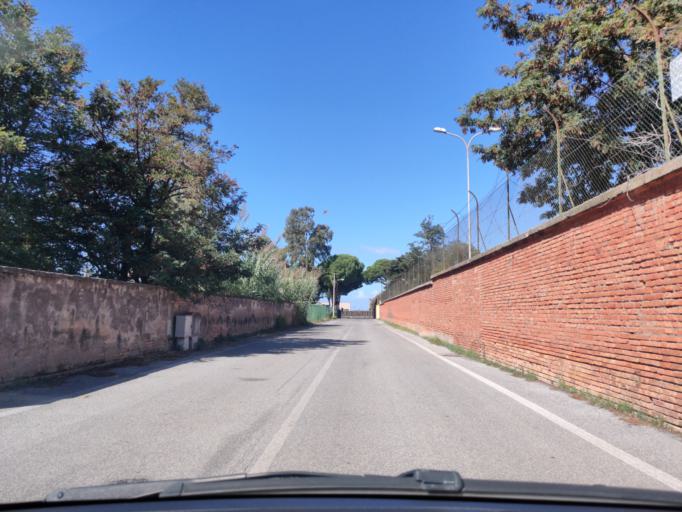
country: IT
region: Latium
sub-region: Citta metropolitana di Roma Capitale
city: Aurelia
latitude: 42.1396
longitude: 11.7867
